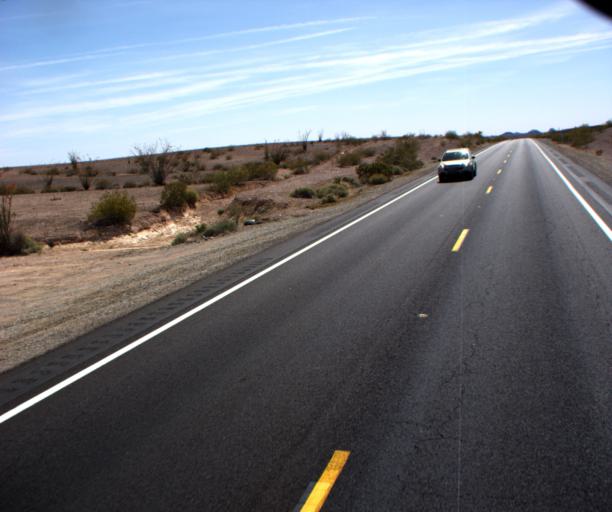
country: US
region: Arizona
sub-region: Yuma County
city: Wellton
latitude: 33.1067
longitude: -114.2965
